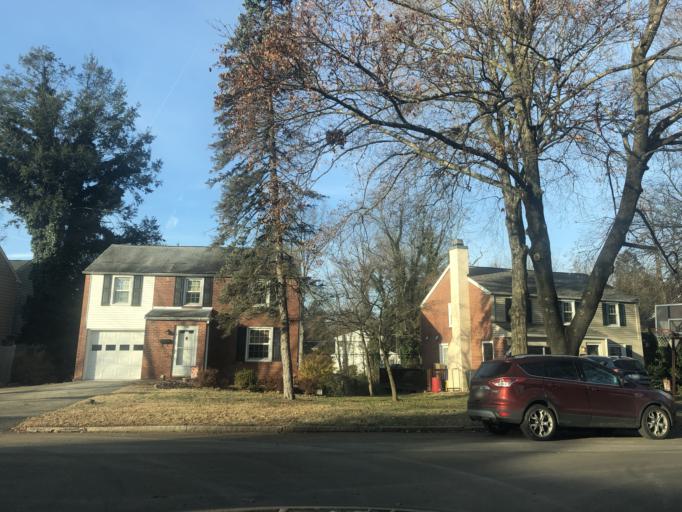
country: US
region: Pennsylvania
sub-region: Delaware County
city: Radnor
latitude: 40.0276
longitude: -75.3418
